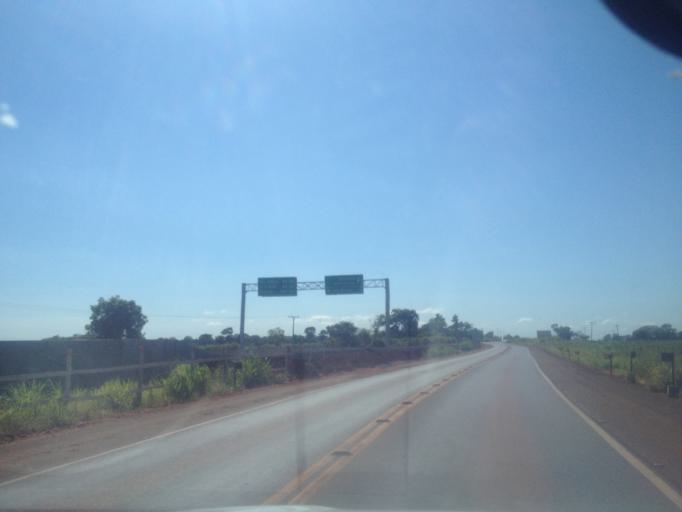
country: BR
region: Minas Gerais
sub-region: Santa Vitoria
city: Santa Vitoria
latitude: -18.9879
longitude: -50.5771
